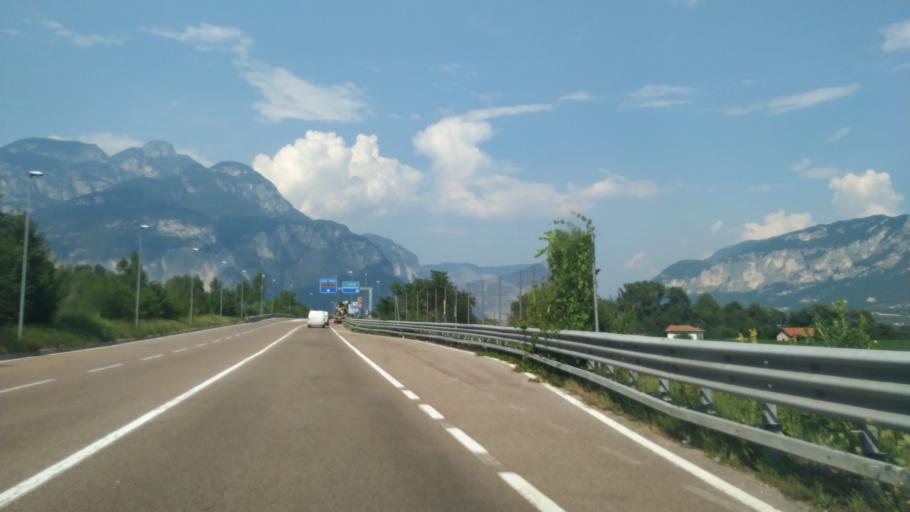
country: IT
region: Trentino-Alto Adige
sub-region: Provincia di Trento
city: Nave San Rocco
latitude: 46.1853
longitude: 11.0986
